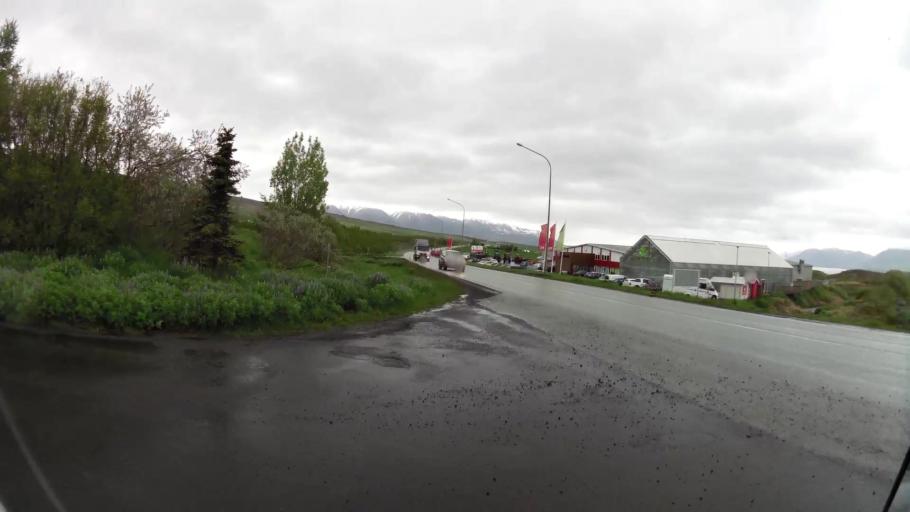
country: IS
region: Northeast
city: Akureyri
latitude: 65.7026
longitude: -18.1511
